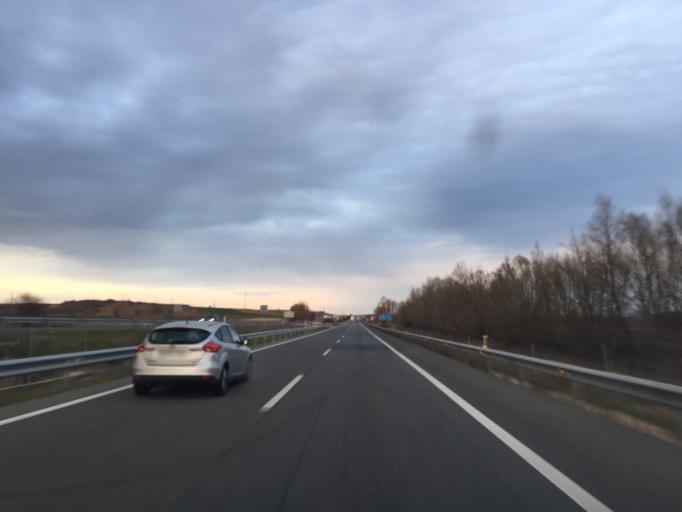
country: ES
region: Castille and Leon
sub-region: Provincia de Burgos
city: Celada del Camino
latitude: 42.2675
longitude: -3.9217
